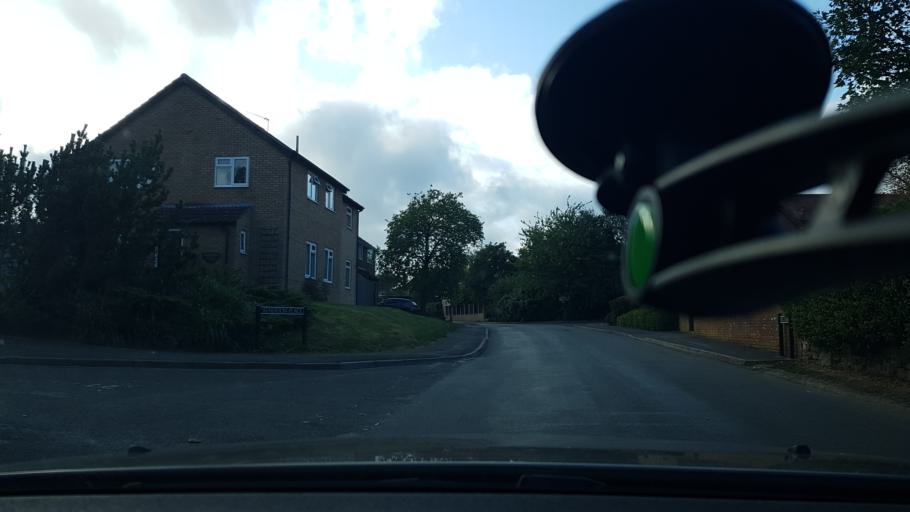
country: GB
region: England
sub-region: West Berkshire
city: Lambourn
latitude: 51.5099
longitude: -1.5305
